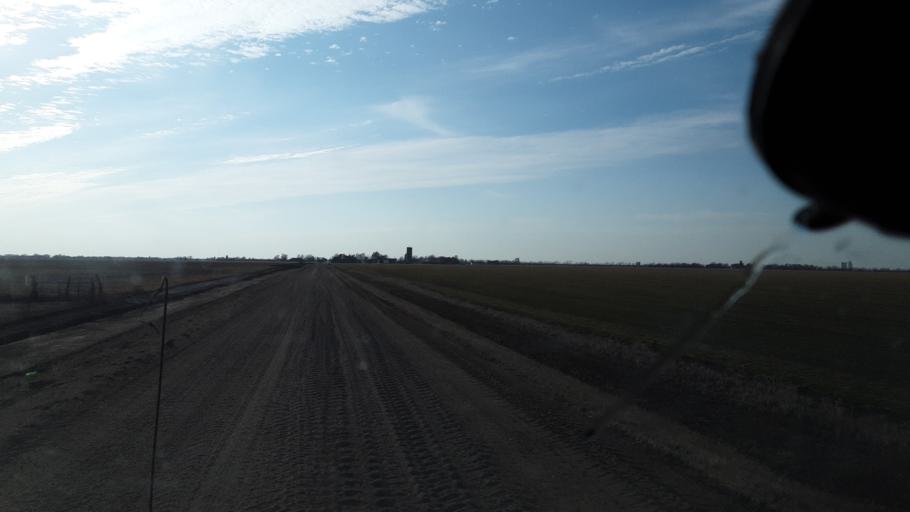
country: US
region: Kansas
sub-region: Reno County
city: South Hutchinson
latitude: 37.9842
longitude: -97.9780
